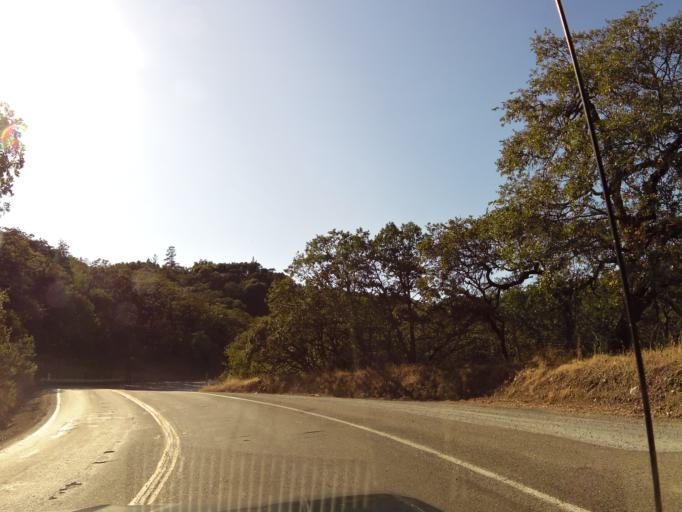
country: US
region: California
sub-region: Sonoma County
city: Cloverdale
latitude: 38.8405
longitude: -123.0589
